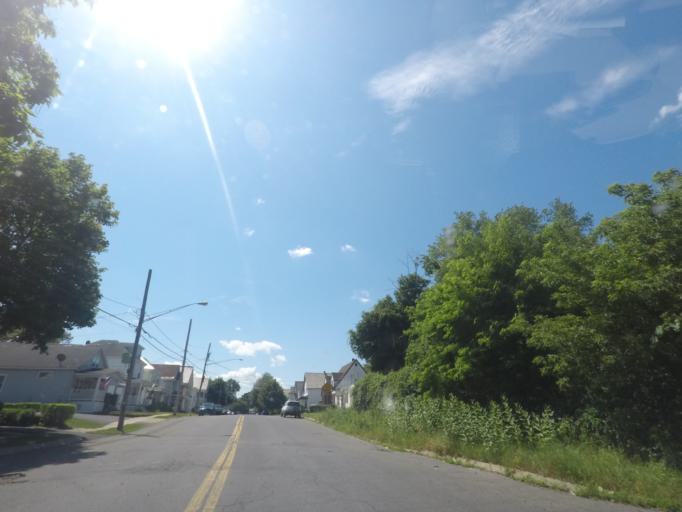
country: US
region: New York
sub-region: Schenectady County
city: Rotterdam
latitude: 42.7956
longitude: -73.9583
